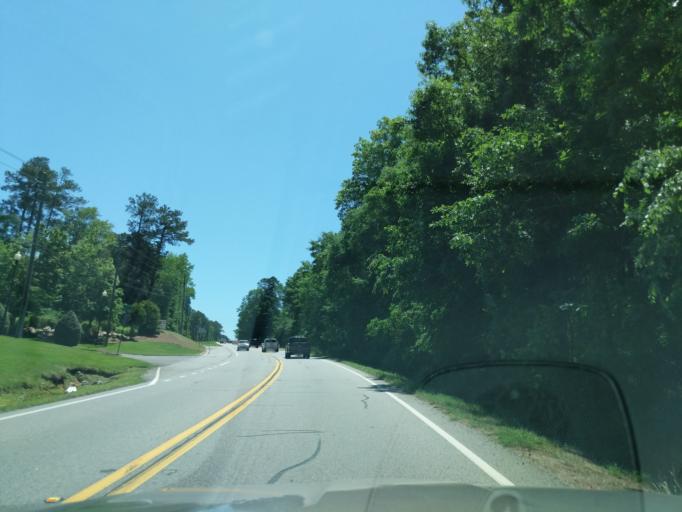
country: US
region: Georgia
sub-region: Columbia County
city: Evans
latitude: 33.5602
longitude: -82.1024
